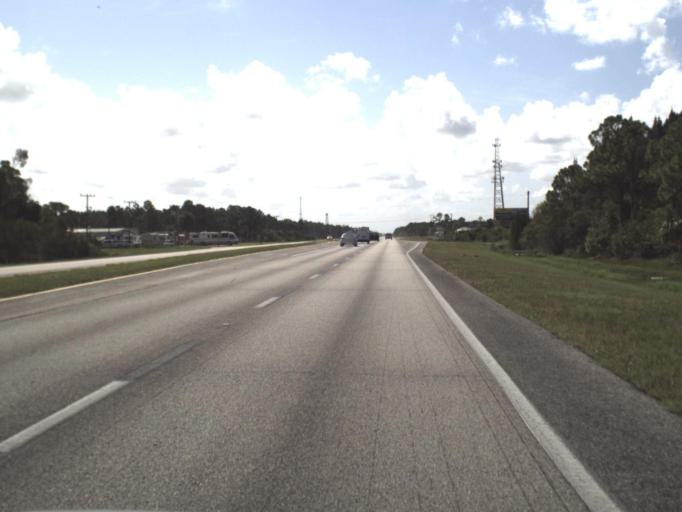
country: US
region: Florida
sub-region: Charlotte County
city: Charlotte Park
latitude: 26.8457
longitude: -81.9800
